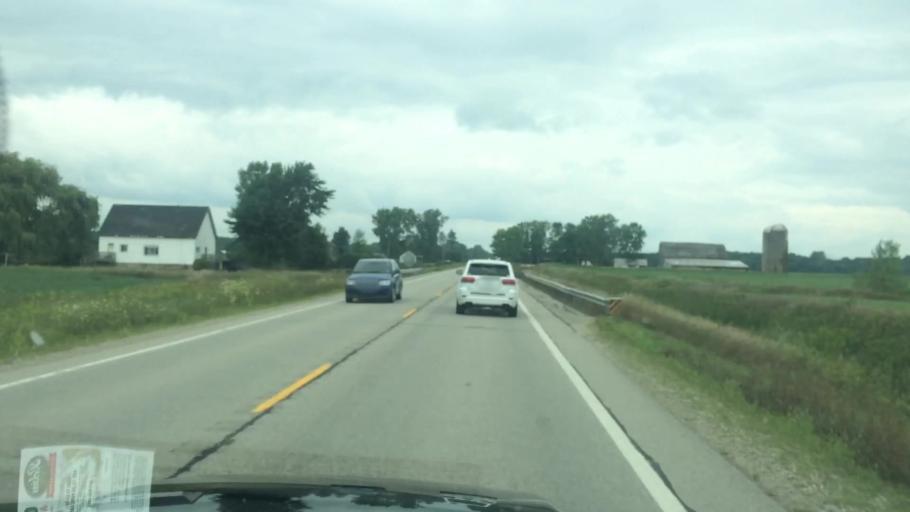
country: US
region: Michigan
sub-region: Tuscola County
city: Cass City
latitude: 43.4788
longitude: -83.0905
